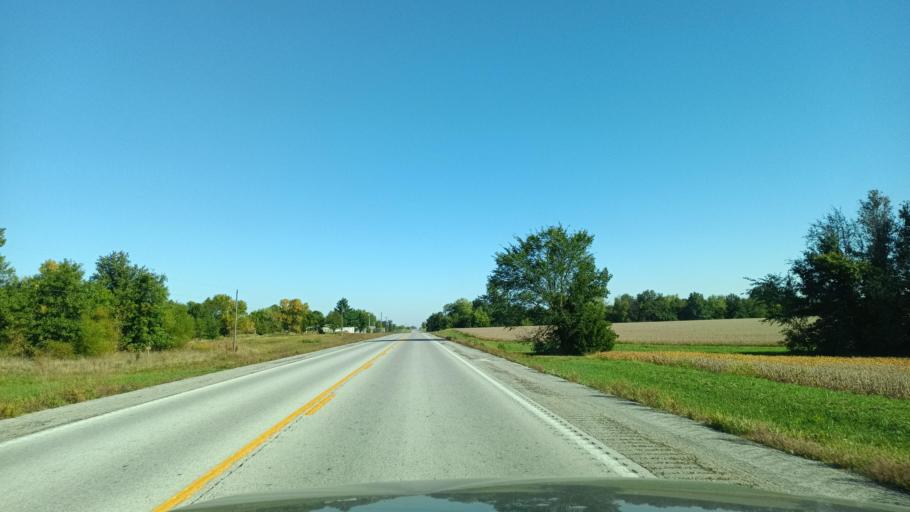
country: US
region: Missouri
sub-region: Audrain County
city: Vandalia
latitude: 39.3422
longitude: -91.6429
